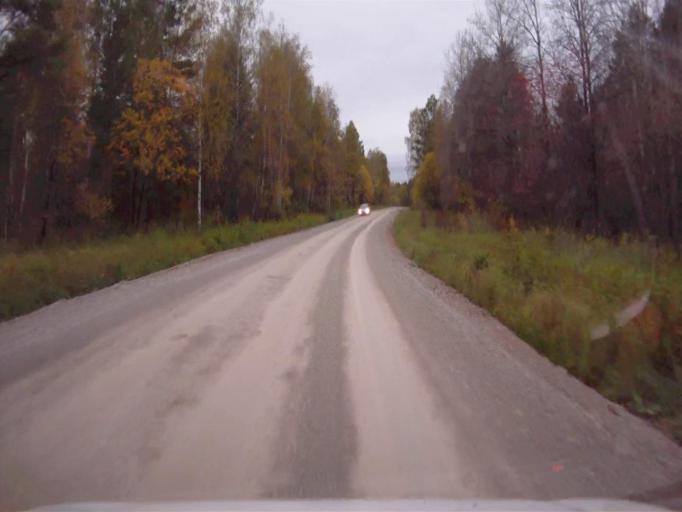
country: RU
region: Chelyabinsk
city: Nyazepetrovsk
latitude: 56.0636
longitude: 59.4431
